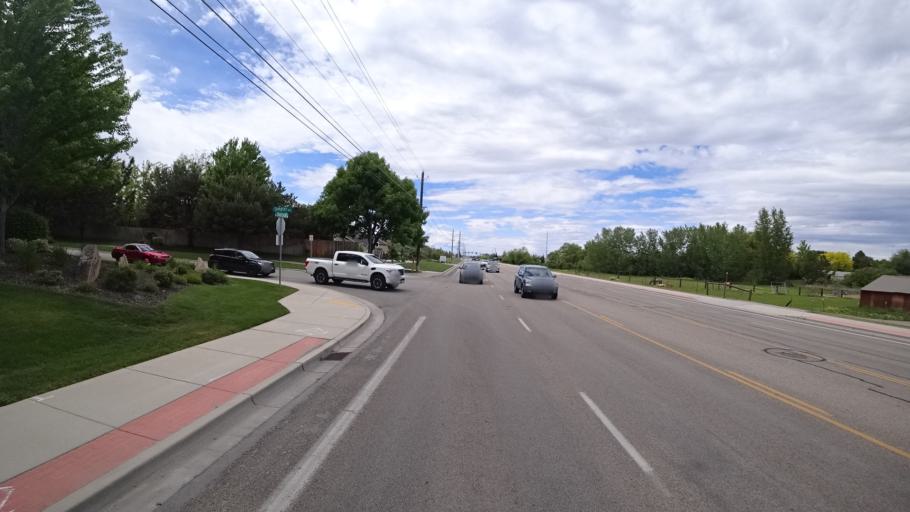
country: US
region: Idaho
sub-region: Ada County
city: Meridian
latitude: 43.5902
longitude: -116.3305
